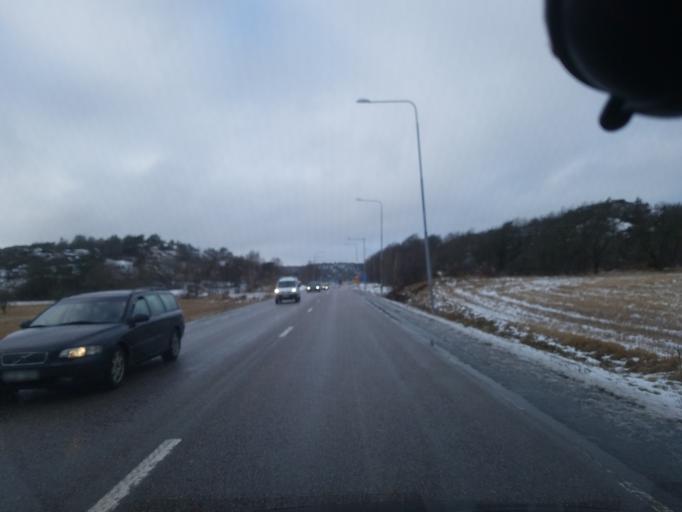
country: SE
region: Vaestra Goetaland
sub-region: Lysekils Kommun
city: Brastad
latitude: 58.2975
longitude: 11.5402
